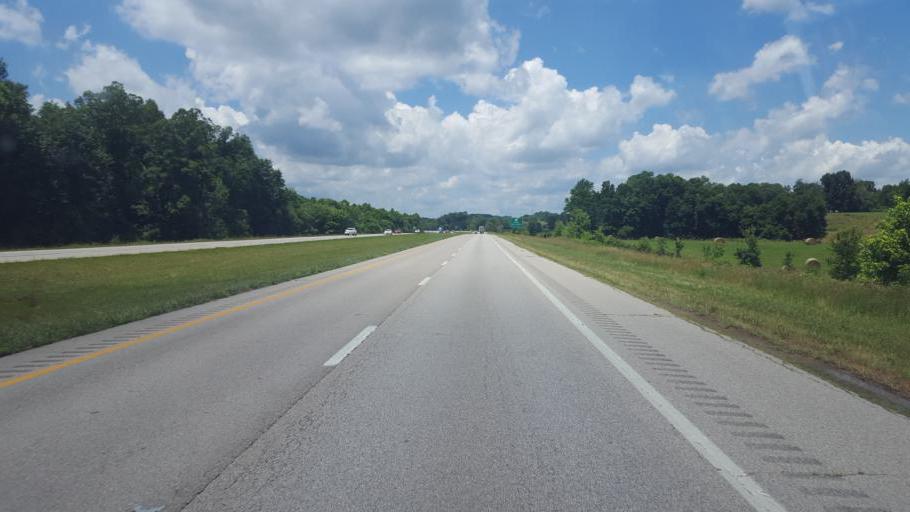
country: US
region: Ohio
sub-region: Gallia County
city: Gallipolis
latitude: 38.8939
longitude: -82.3675
